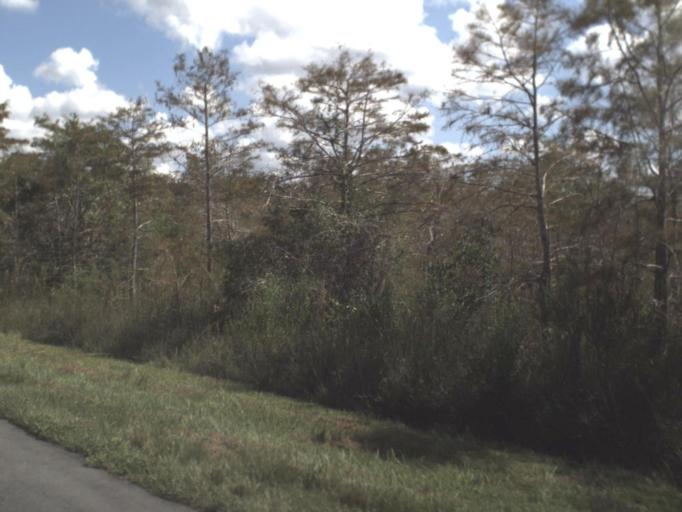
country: US
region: Florida
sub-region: Miami-Dade County
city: Kendall West
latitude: 25.8500
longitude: -80.9659
